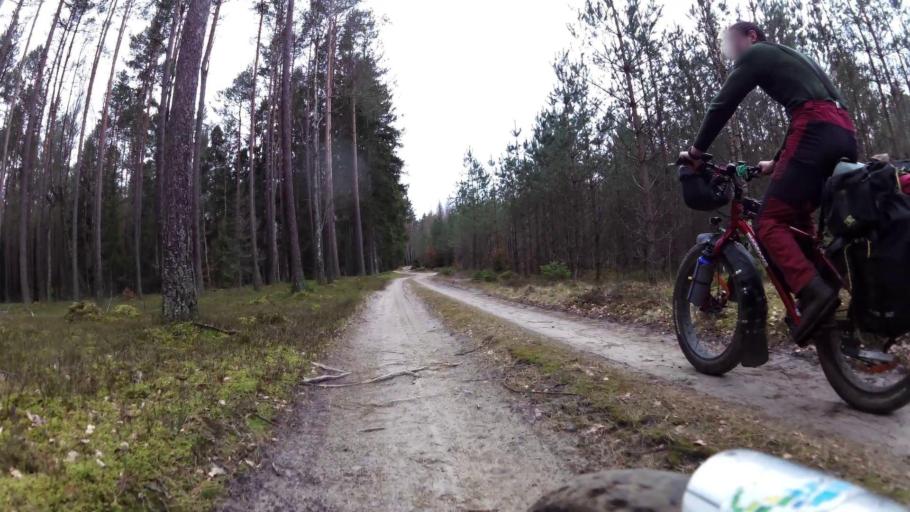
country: PL
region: Pomeranian Voivodeship
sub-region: Powiat bytowski
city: Trzebielino
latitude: 54.1452
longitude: 17.1551
